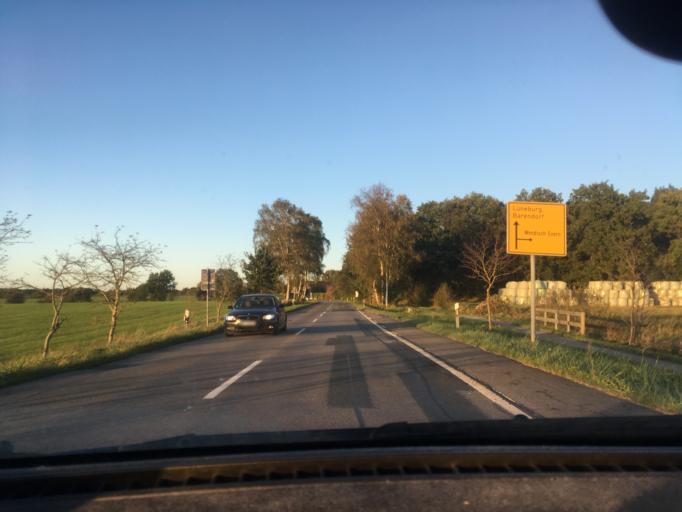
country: DE
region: Lower Saxony
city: Wendisch Evern
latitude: 53.2098
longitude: 10.4635
